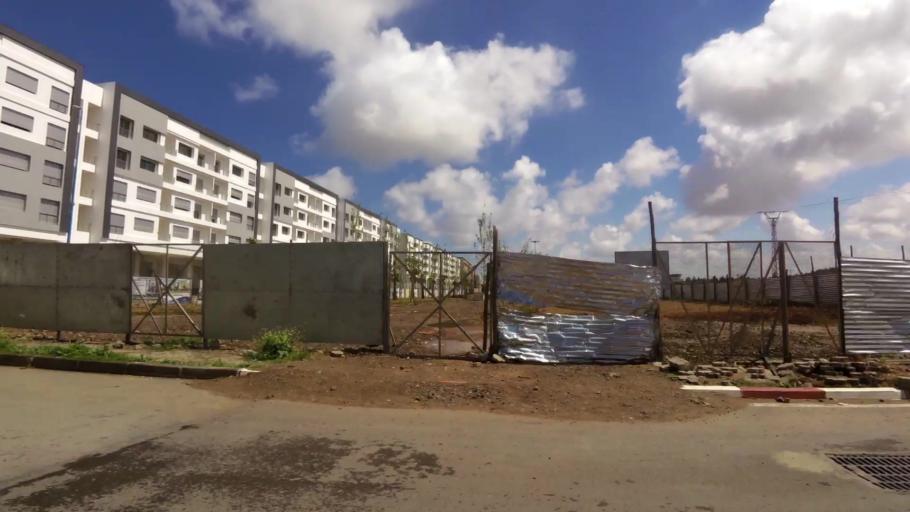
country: MA
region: Grand Casablanca
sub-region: Nouaceur
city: Dar Bouazza
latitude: 33.5285
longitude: -7.7343
